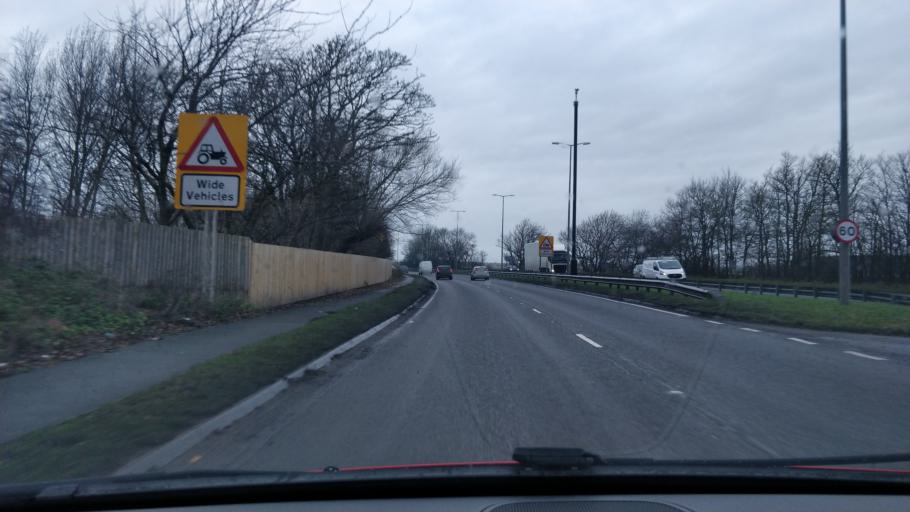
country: GB
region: England
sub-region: Sefton
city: Ince Blundell
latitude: 53.5276
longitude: -3.0326
